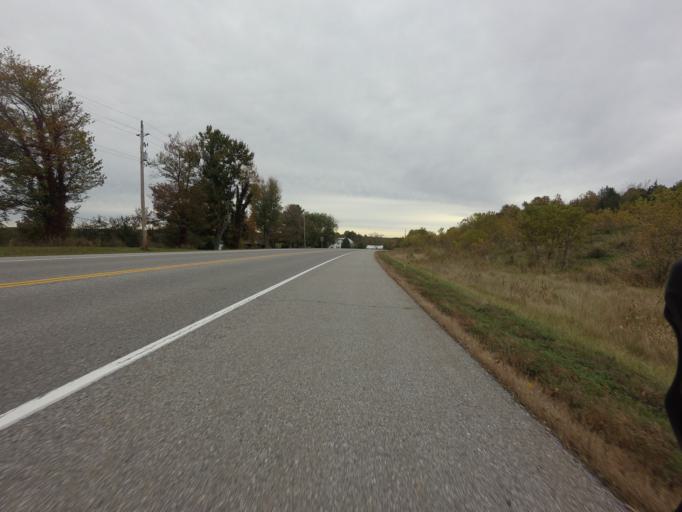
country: CA
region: Ontario
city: Gananoque
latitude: 44.4563
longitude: -76.2673
